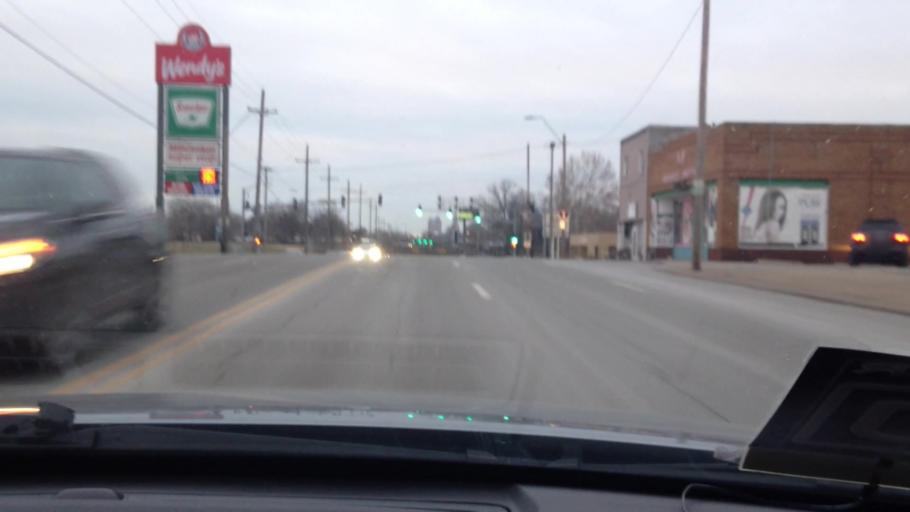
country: US
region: Missouri
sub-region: Jackson County
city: Kansas City
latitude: 39.0942
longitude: -94.5367
